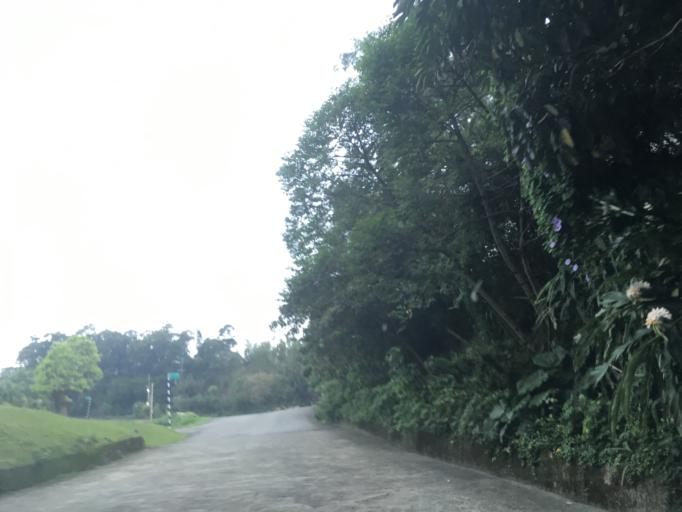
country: TW
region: Taiwan
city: Daxi
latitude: 24.8849
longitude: 121.3004
